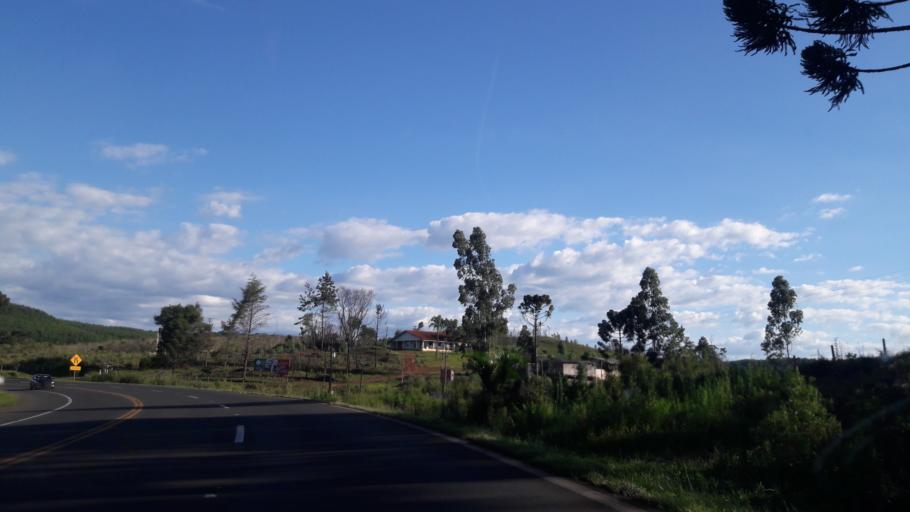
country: BR
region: Parana
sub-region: Guarapuava
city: Guarapuava
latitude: -25.3649
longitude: -51.3494
